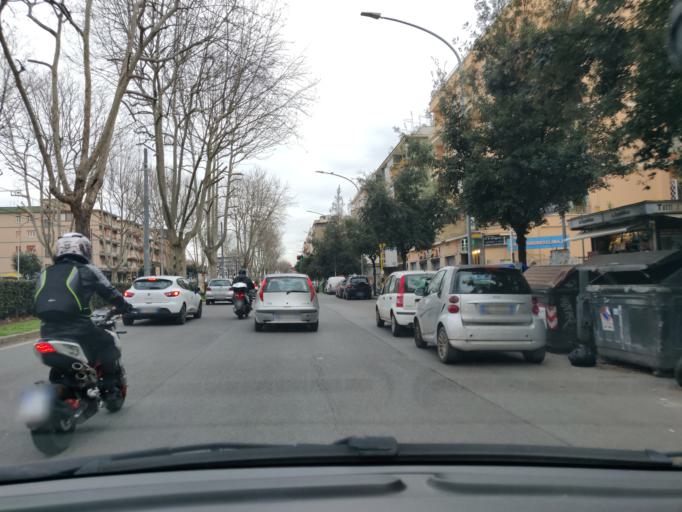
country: VA
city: Vatican City
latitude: 41.8765
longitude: 12.4439
